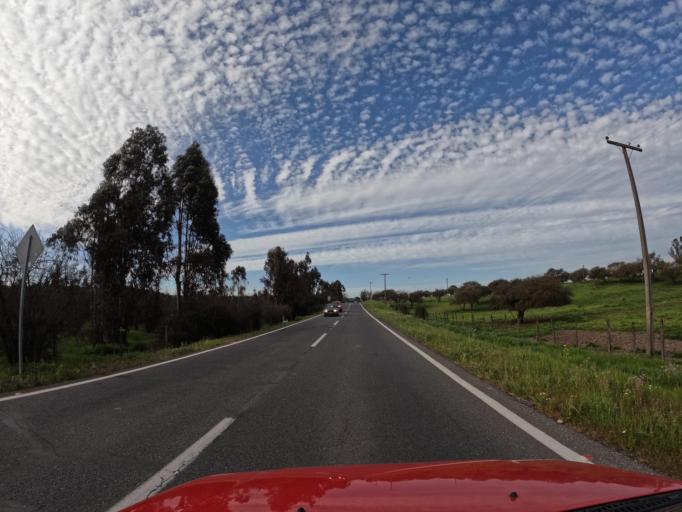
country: CL
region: O'Higgins
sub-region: Provincia de Colchagua
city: Santa Cruz
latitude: -34.2292
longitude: -71.7258
